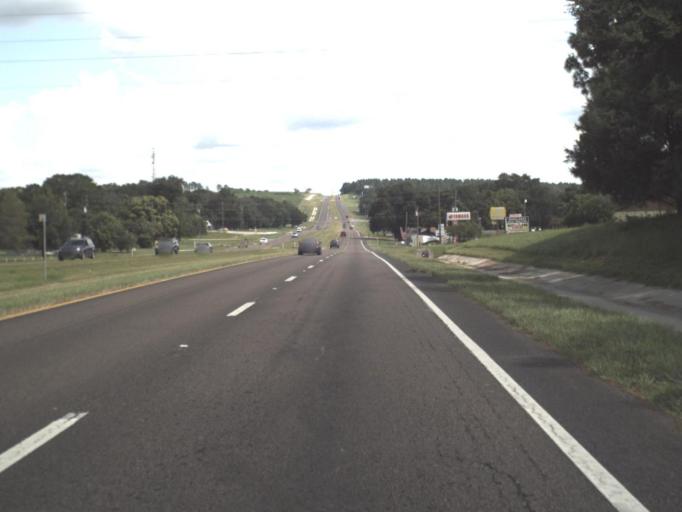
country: US
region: Florida
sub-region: Pasco County
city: Zephyrhills North
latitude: 28.2842
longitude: -82.1877
